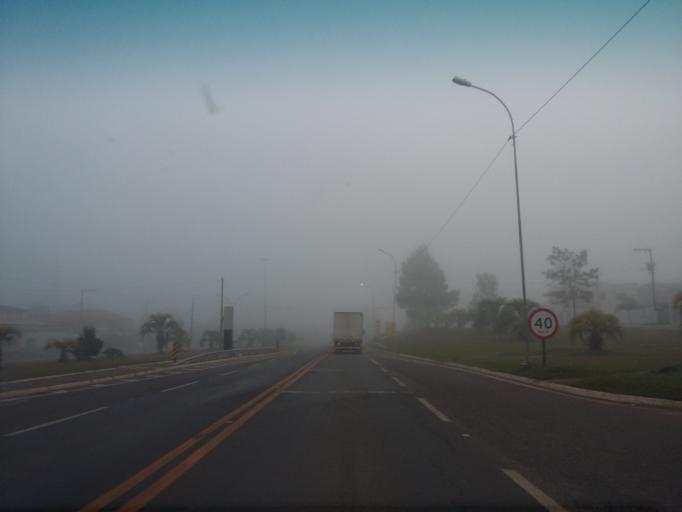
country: BR
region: Santa Catarina
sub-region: Curitibanos
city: Curitibanos
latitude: -27.2676
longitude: -50.4415
